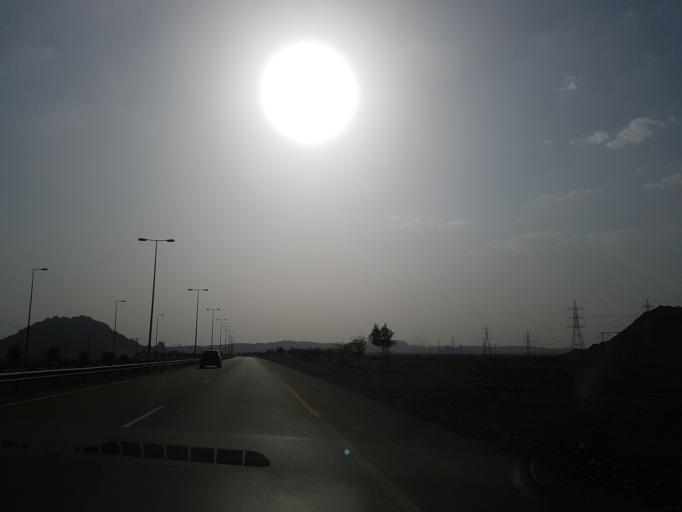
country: OM
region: Al Buraimi
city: Al Buraymi
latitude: 24.2462
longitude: 56.0029
